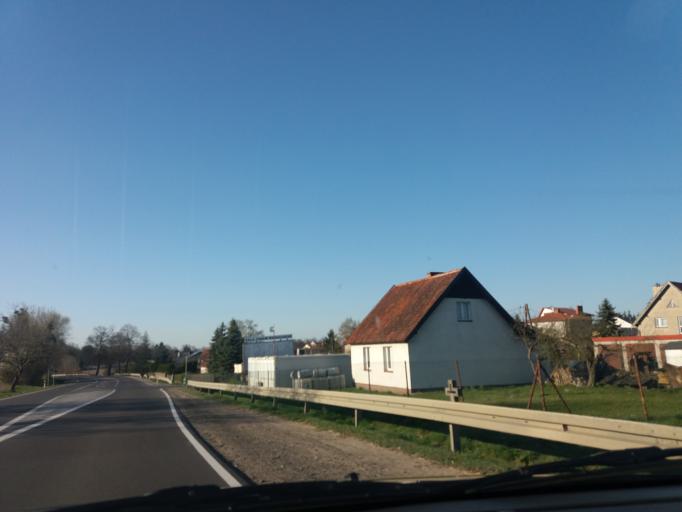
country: PL
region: Warmian-Masurian Voivodeship
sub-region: Powiat nidzicki
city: Nidzica
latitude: 53.3443
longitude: 20.4335
